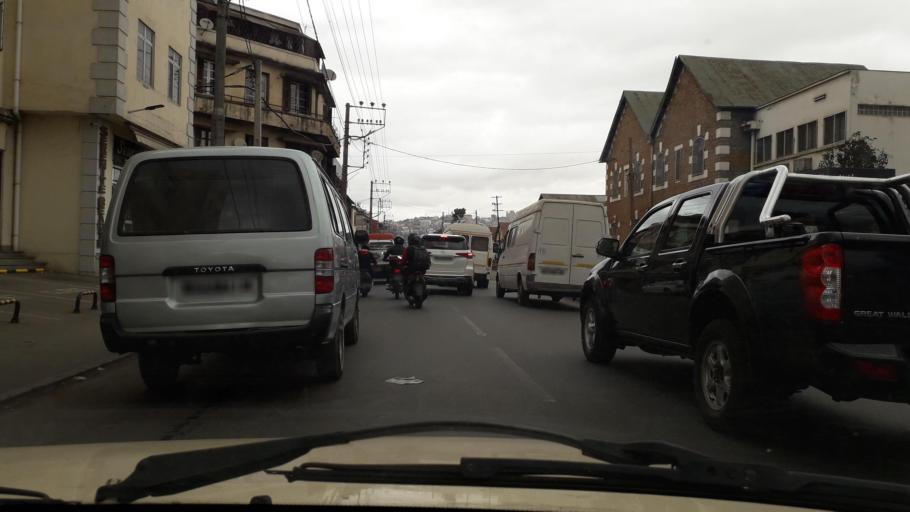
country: MG
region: Analamanga
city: Antananarivo
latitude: -18.8984
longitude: 47.5192
